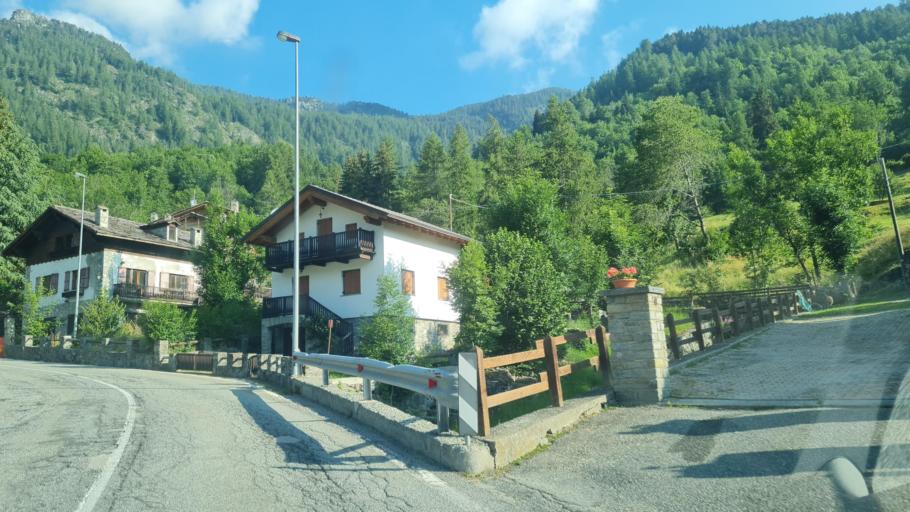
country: IT
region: Aosta Valley
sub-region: Valle d'Aosta
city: Champorcher
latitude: 45.6224
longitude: 7.6404
